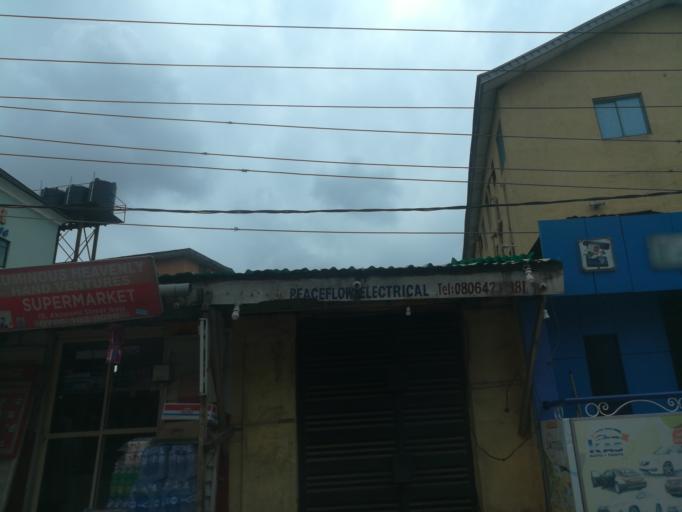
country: NG
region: Lagos
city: Ikeja
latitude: 6.5983
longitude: 3.3376
